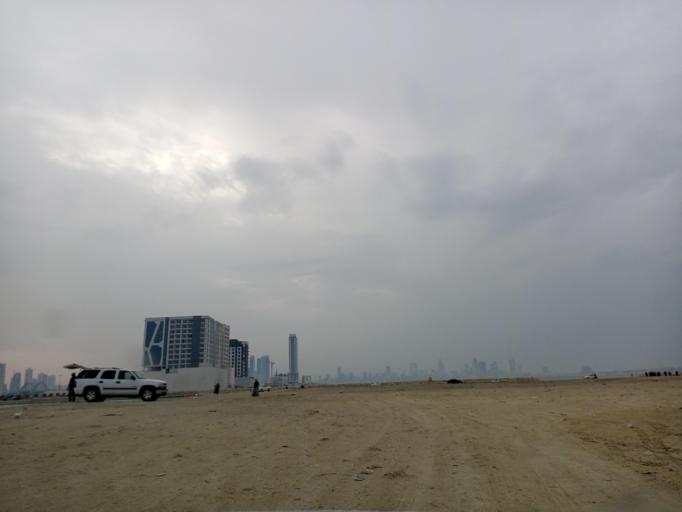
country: BH
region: Muharraq
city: Al Hadd
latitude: 26.2272
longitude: 50.6436
